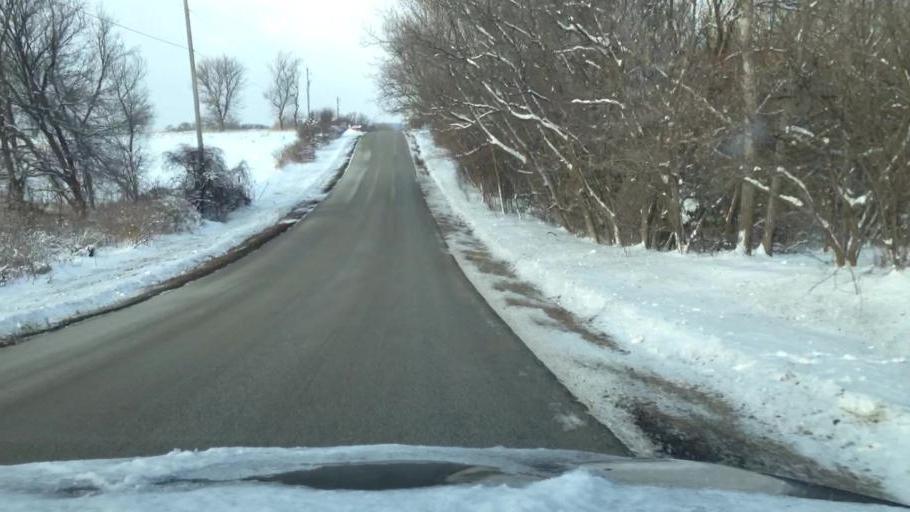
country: US
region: Wisconsin
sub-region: Walworth County
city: East Troy
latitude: 42.8236
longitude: -88.4245
